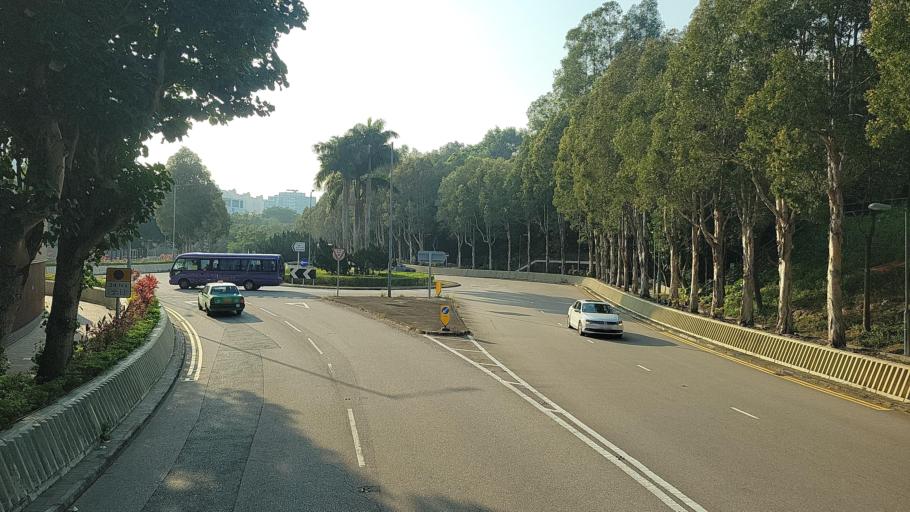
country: HK
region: Tuen Mun
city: Tuen Mun
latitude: 22.3756
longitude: 113.9993
